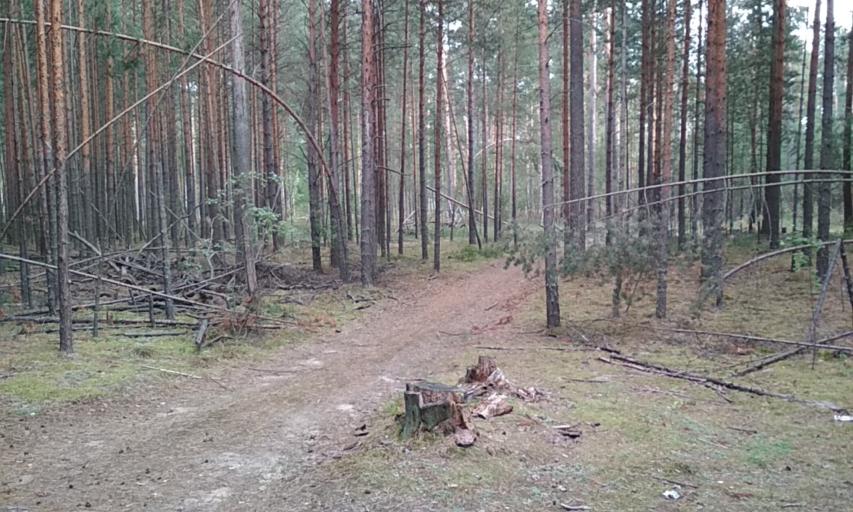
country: RU
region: Tomsk
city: Timiryazevskoye
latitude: 56.4369
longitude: 84.8519
